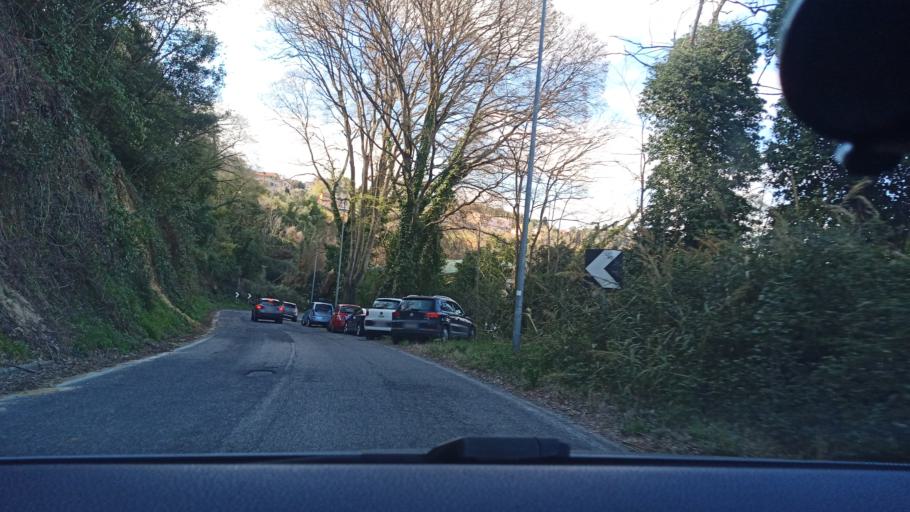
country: IT
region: Latium
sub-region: Citta metropolitana di Roma Capitale
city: Torrita Tiberina
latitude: 42.2391
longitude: 12.6181
